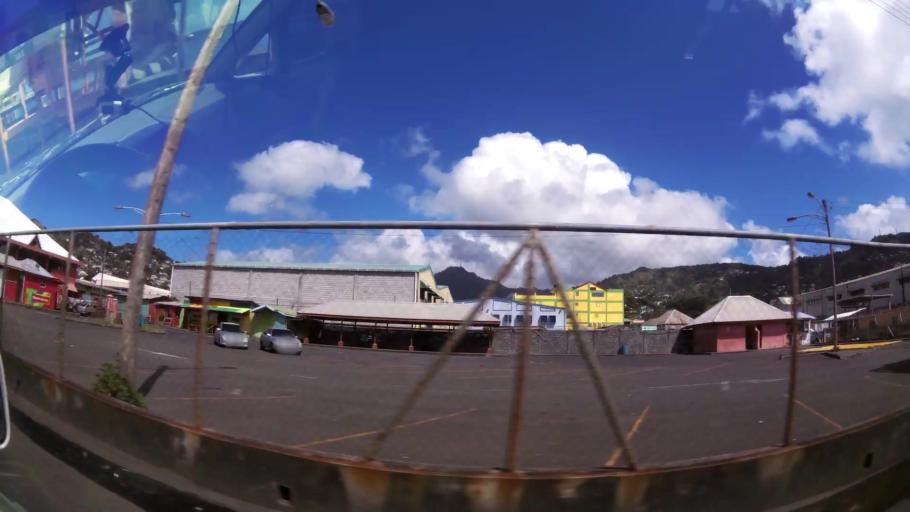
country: VC
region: Saint George
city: Kingstown
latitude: 13.1550
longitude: -61.2287
